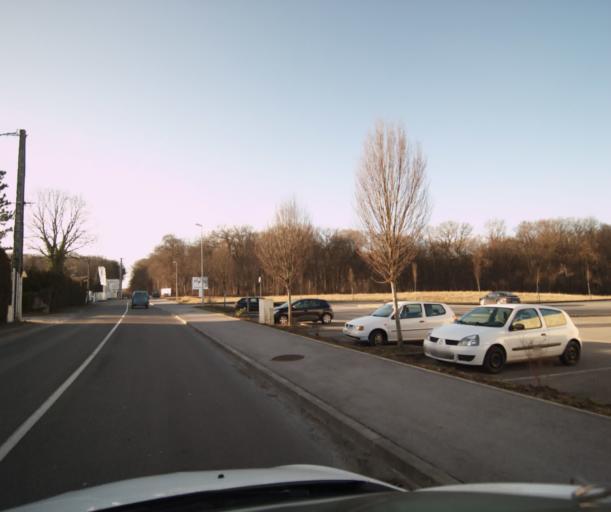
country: FR
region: Franche-Comte
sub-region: Departement du Doubs
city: Franois
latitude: 47.2187
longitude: 5.9439
